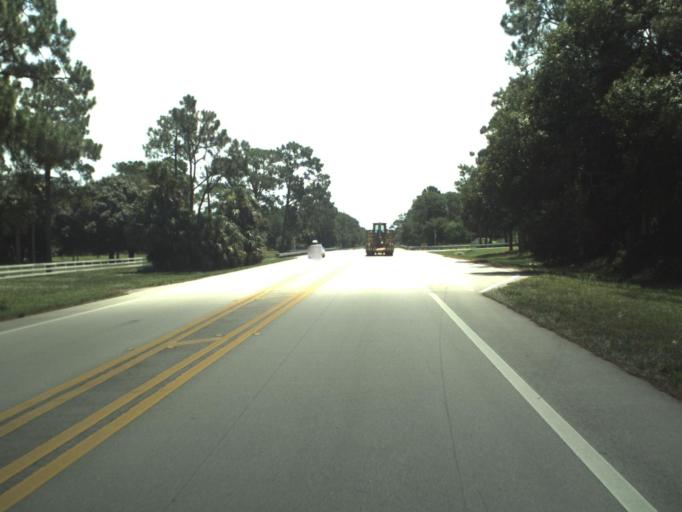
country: US
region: Florida
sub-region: Martin County
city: Palm City
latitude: 27.0496
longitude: -80.3377
